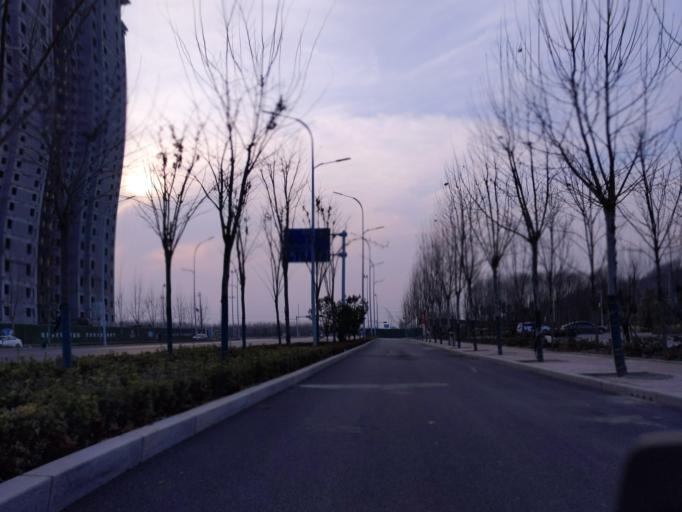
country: CN
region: Henan Sheng
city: Puyang
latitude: 35.8181
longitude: 115.0097
